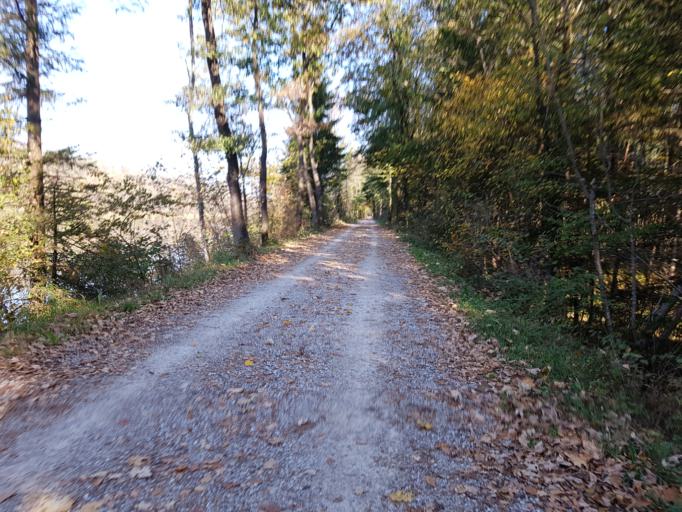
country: AT
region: Salzburg
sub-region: Politischer Bezirk Hallein
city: Puch bei Hallein
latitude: 47.7131
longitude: 13.0810
